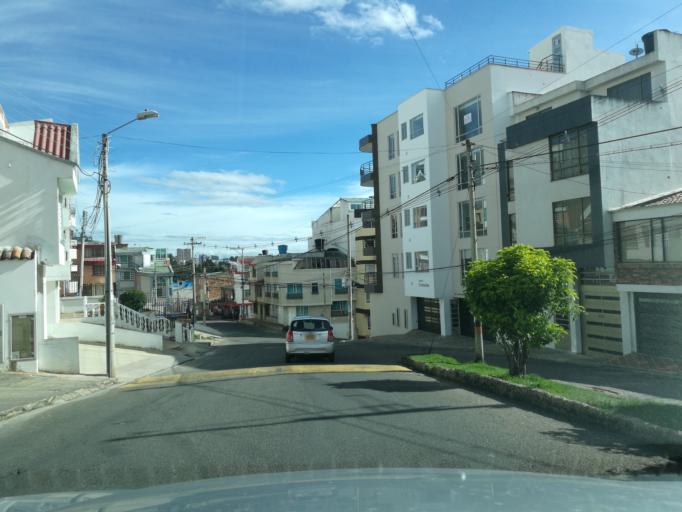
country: CO
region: Boyaca
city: Tunja
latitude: 5.5553
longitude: -73.3527
